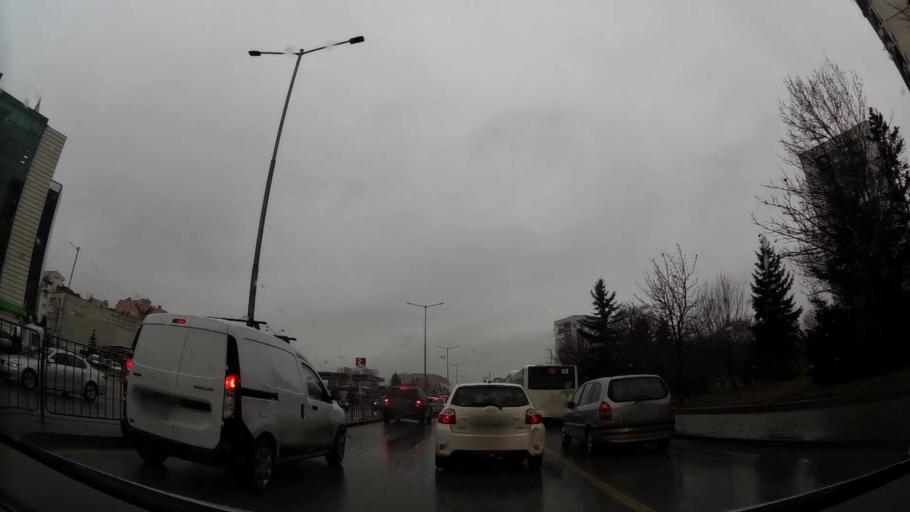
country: BG
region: Sofia-Capital
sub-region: Stolichna Obshtina
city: Sofia
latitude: 42.6508
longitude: 23.3787
